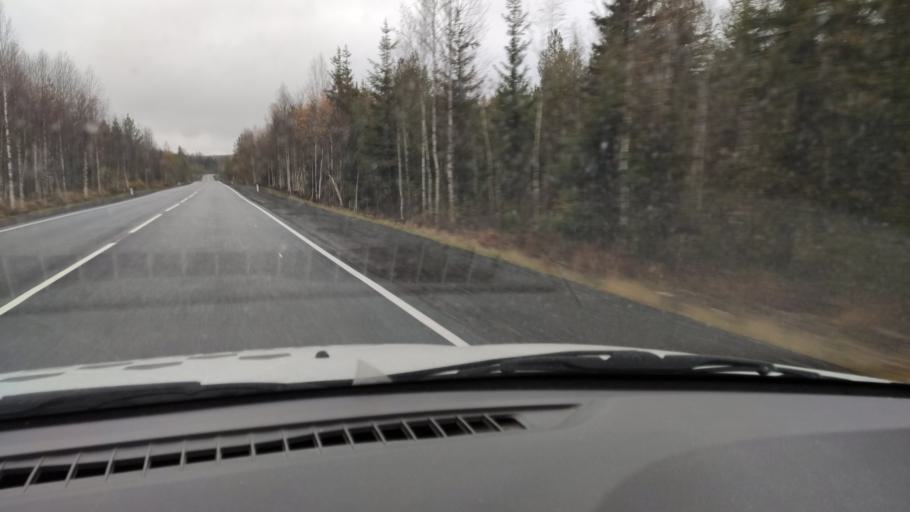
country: RU
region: Kirov
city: Chernaya Kholunitsa
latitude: 58.8740
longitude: 51.5026
